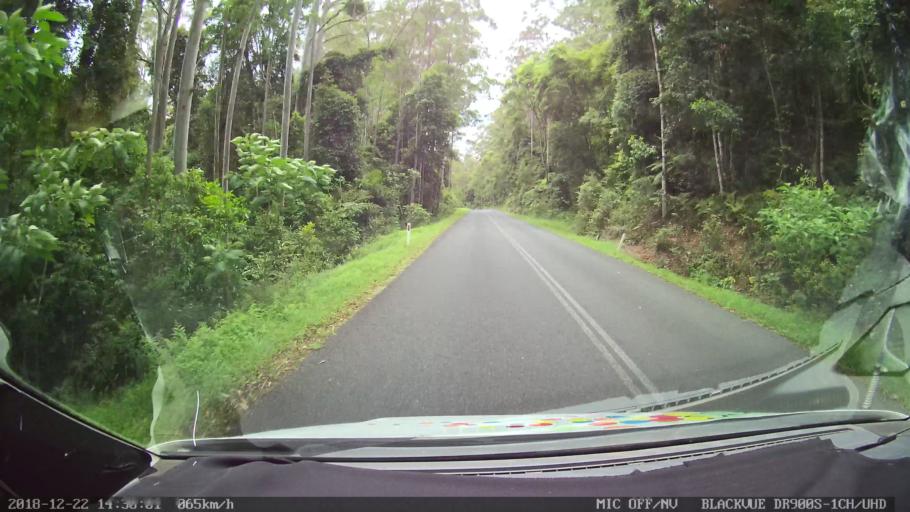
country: AU
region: New South Wales
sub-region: Bellingen
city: Dorrigo
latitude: -30.0820
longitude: 152.6335
